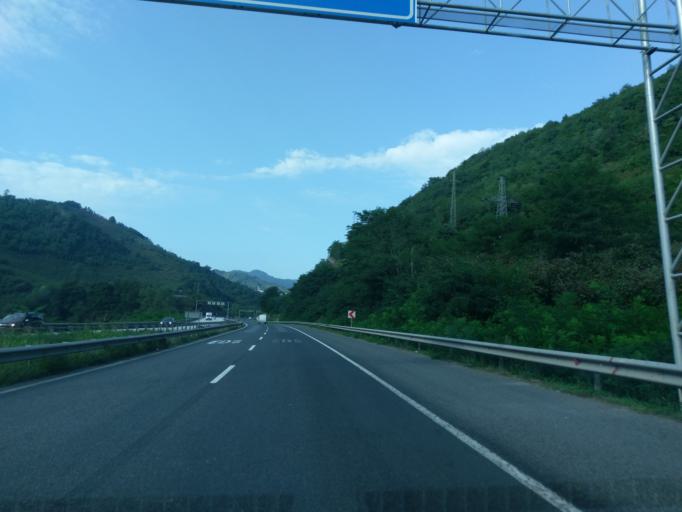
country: TR
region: Ordu
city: Persembe
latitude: 40.9854
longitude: 37.7755
